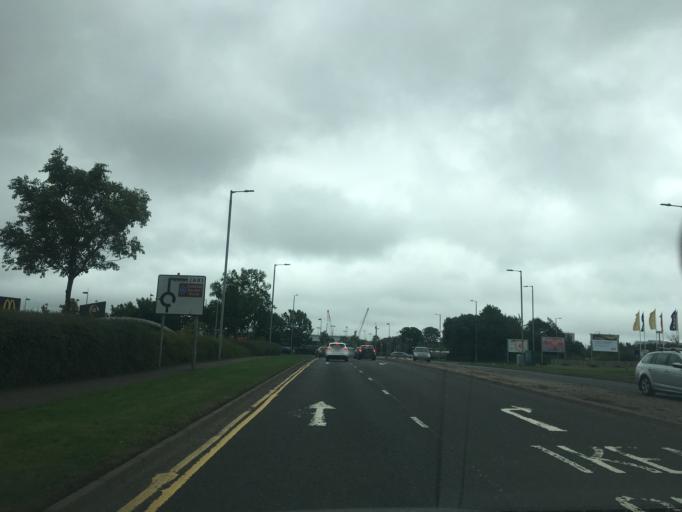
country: GB
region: Scotland
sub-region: Renfrewshire
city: Renfrew
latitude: 55.8726
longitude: -4.3616
